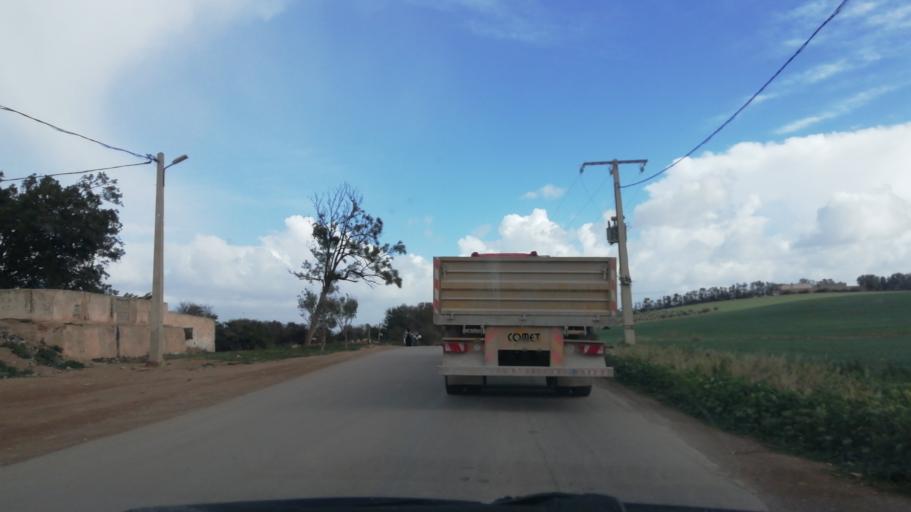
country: DZ
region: Oran
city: Sidi ech Chahmi
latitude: 35.6423
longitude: -0.5162
